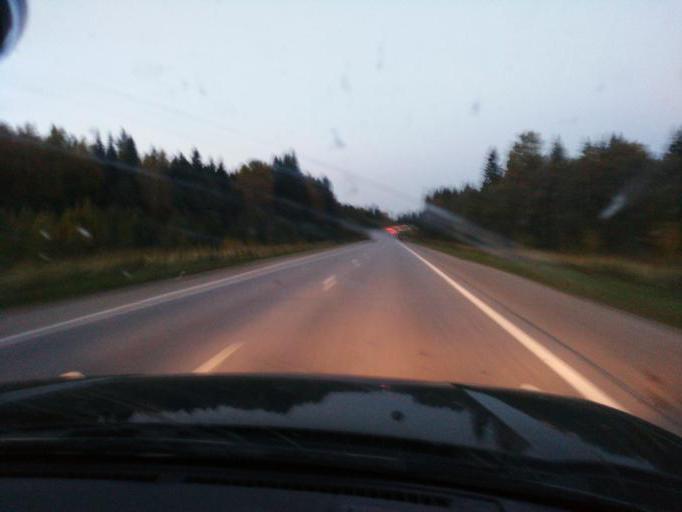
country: RU
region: Perm
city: Kalino
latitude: 58.2764
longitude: 57.3938
